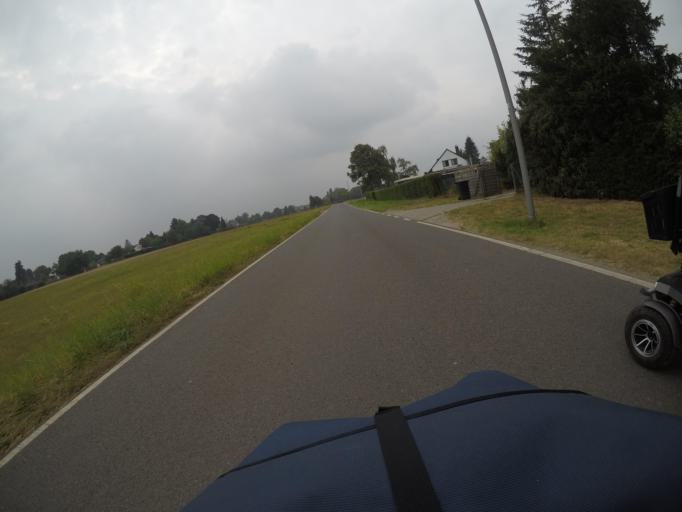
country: DE
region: North Rhine-Westphalia
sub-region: Regierungsbezirk Dusseldorf
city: Krefeld
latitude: 51.2982
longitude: 6.6141
